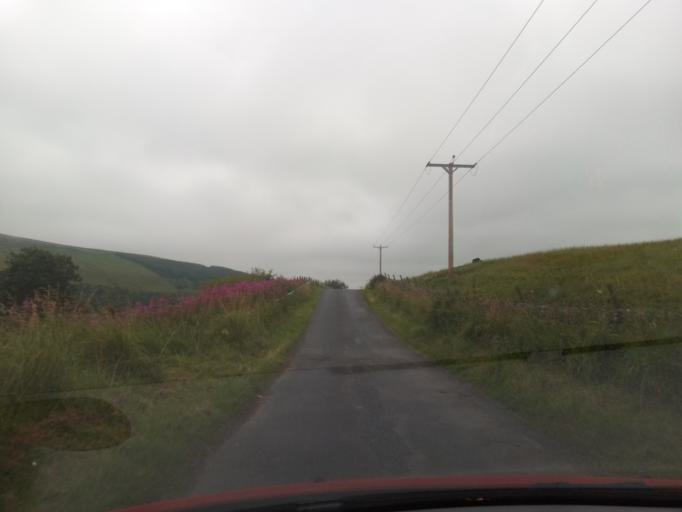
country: GB
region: Scotland
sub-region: The Scottish Borders
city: Galashiels
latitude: 55.6827
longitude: -2.8728
